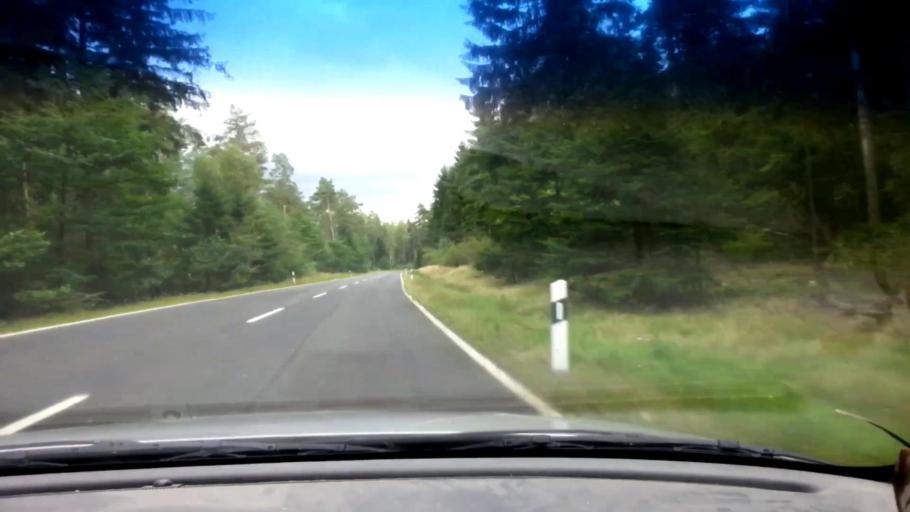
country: DE
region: Bavaria
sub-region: Upper Palatinate
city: Waldsassen
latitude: 50.0209
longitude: 12.3112
